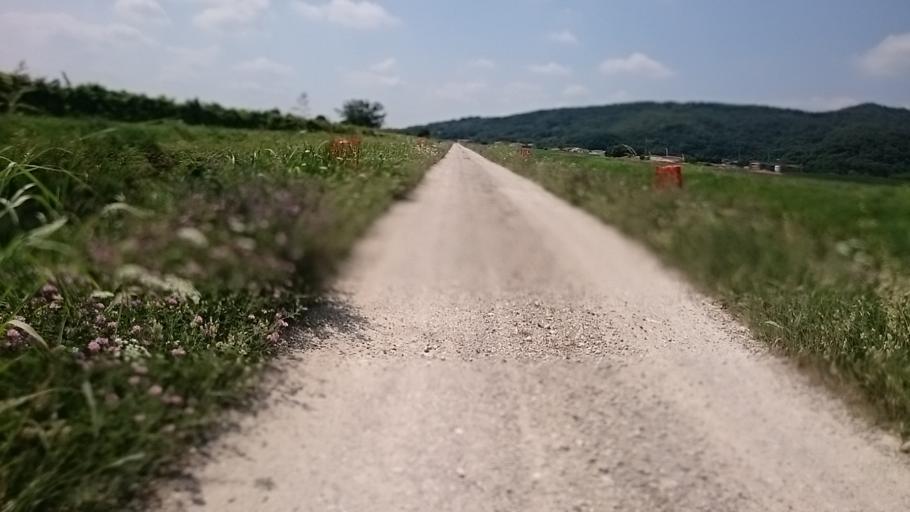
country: IT
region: Veneto
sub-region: Provincia di Padova
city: Montegrotto Terme
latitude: 45.3170
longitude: 11.7954
